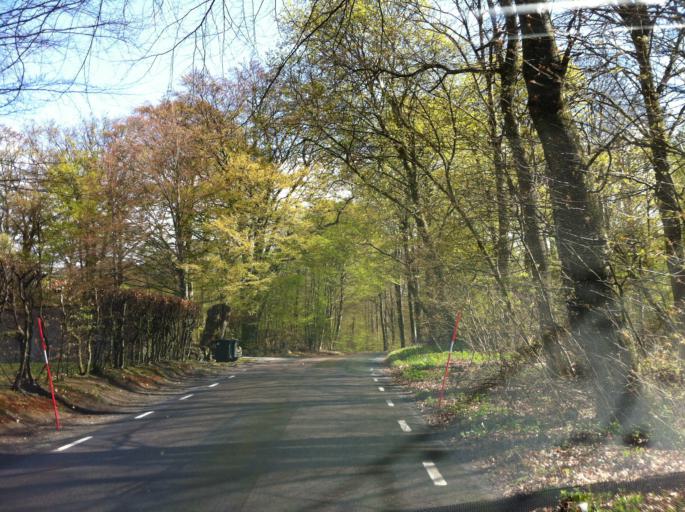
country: SE
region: Skane
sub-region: Horby Kommun
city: Hoerby
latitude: 55.8784
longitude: 13.6368
